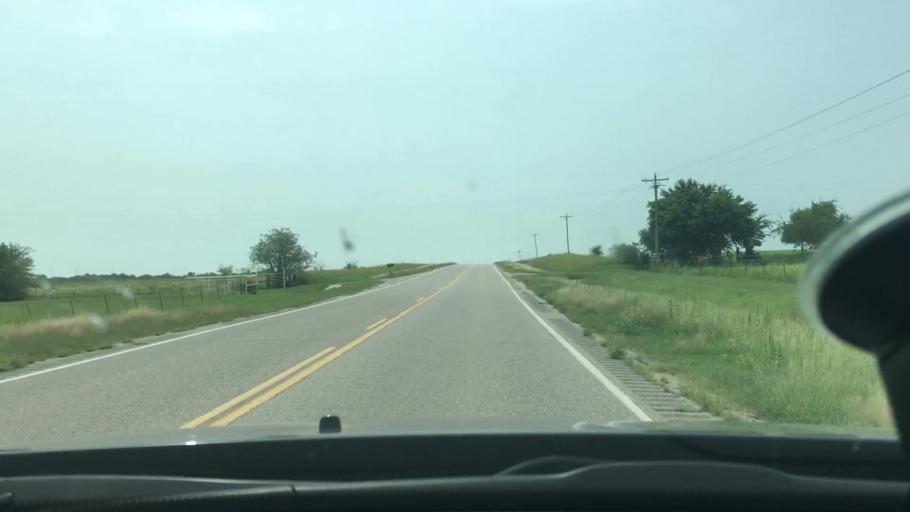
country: US
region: Oklahoma
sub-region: Marshall County
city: Kingston
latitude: 34.0281
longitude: -96.7611
